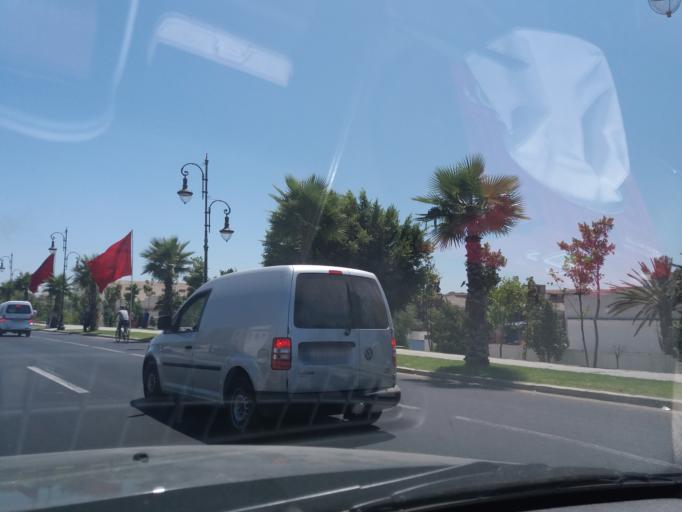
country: MA
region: Tanger-Tetouan
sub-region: Tanger-Assilah
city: Tangier
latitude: 35.7467
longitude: -5.7847
